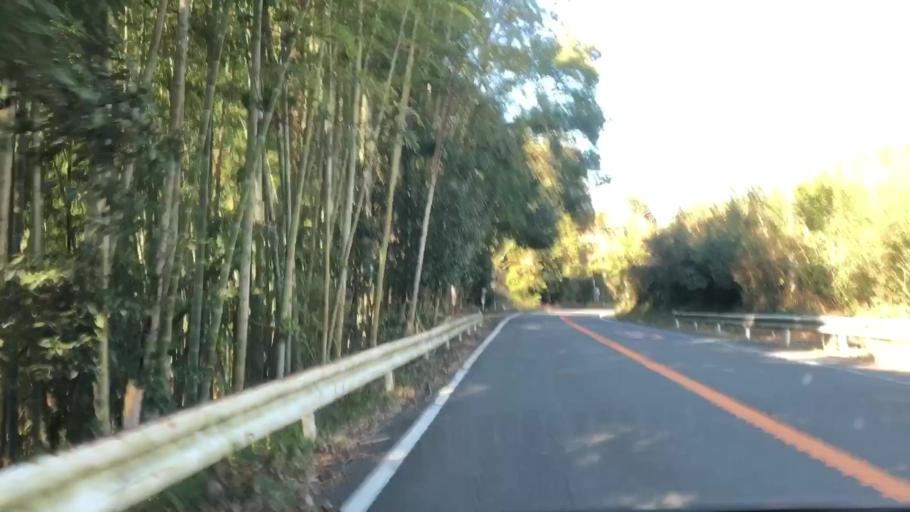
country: JP
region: Kagoshima
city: Satsumasendai
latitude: 31.8547
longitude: 130.4293
